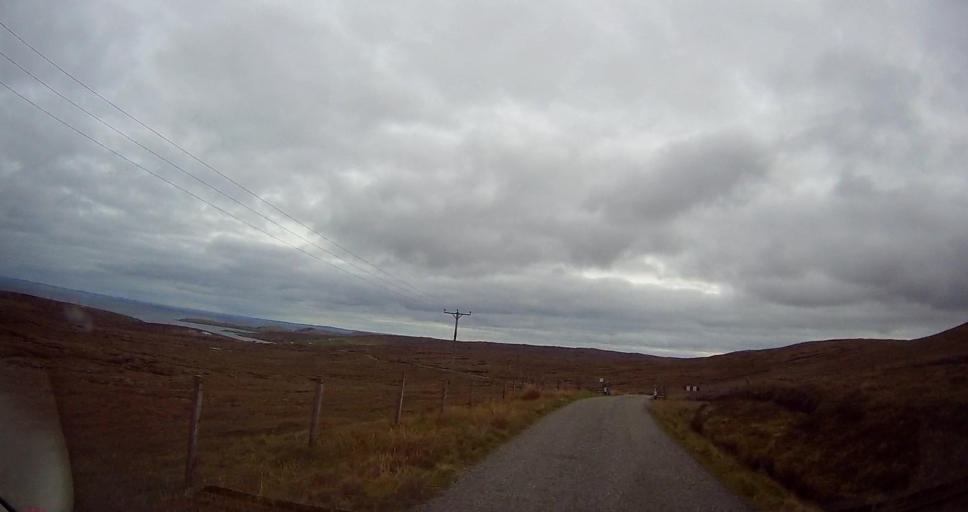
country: GB
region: Scotland
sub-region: Shetland Islands
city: Shetland
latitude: 60.5707
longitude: -1.0667
